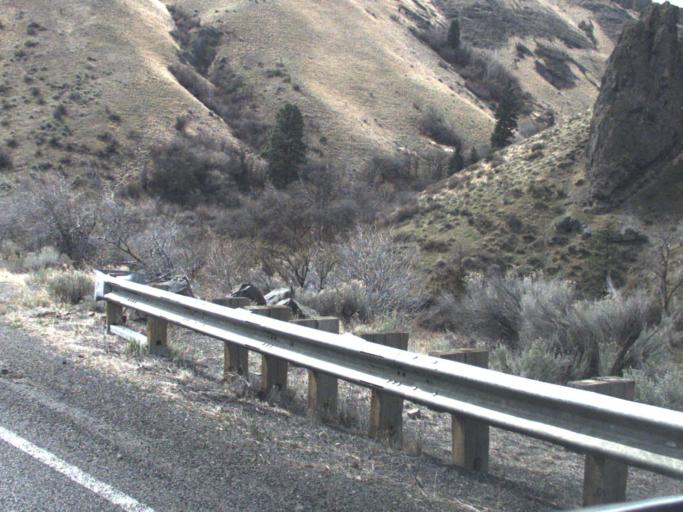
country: US
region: Washington
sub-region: Yakima County
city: Tieton
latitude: 46.7616
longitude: -120.8294
